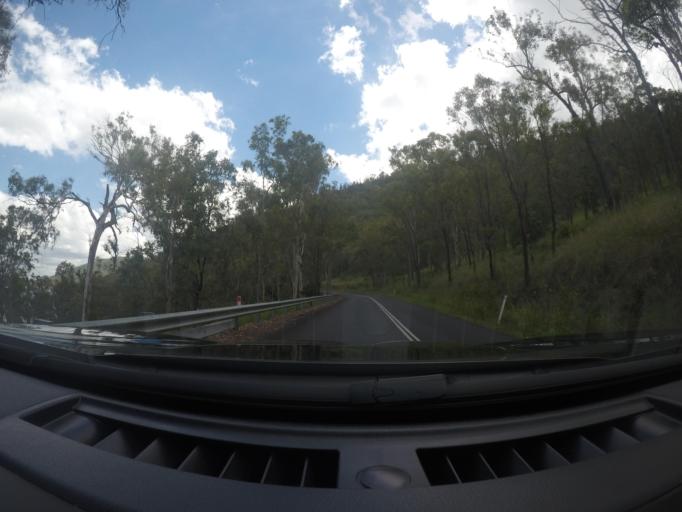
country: AU
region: Queensland
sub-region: Moreton Bay
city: Woodford
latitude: -27.0915
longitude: 152.5625
